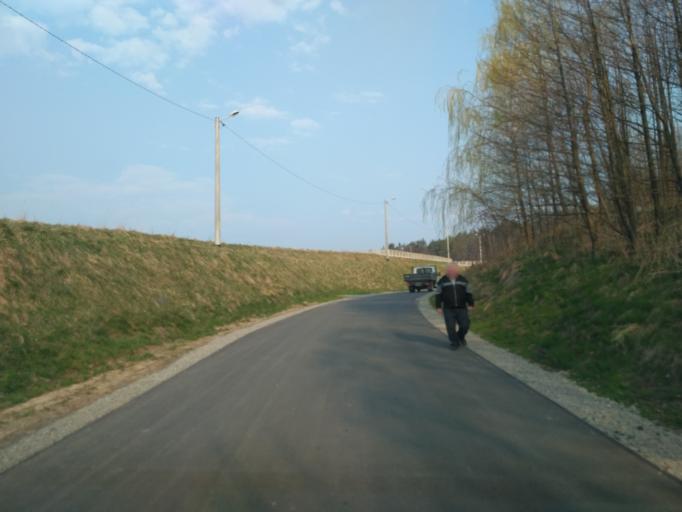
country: PL
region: Subcarpathian Voivodeship
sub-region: Powiat strzyzowski
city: Wisniowa
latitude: 49.8701
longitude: 21.6455
